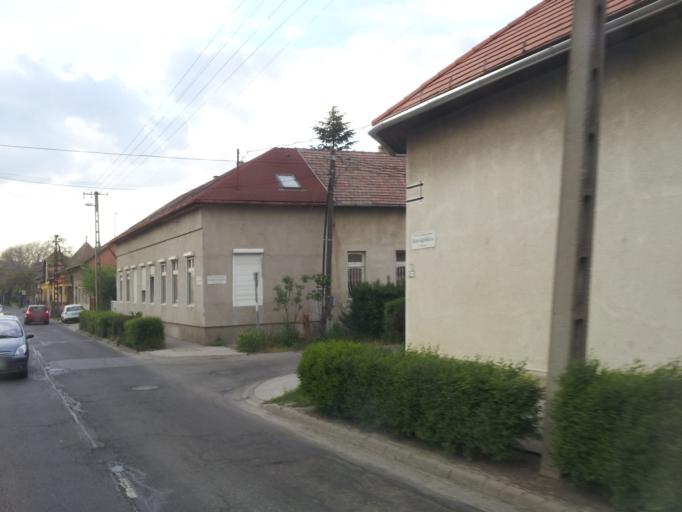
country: HU
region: Budapest
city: Budapest XV. keruelet
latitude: 47.5713
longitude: 19.1272
